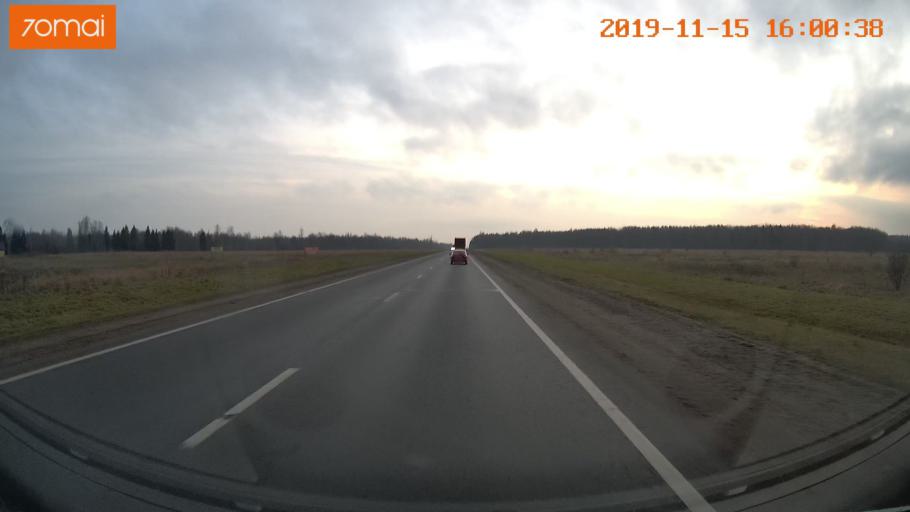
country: RU
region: Jaroslavl
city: Yaroslavl
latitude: 57.7936
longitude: 39.9375
